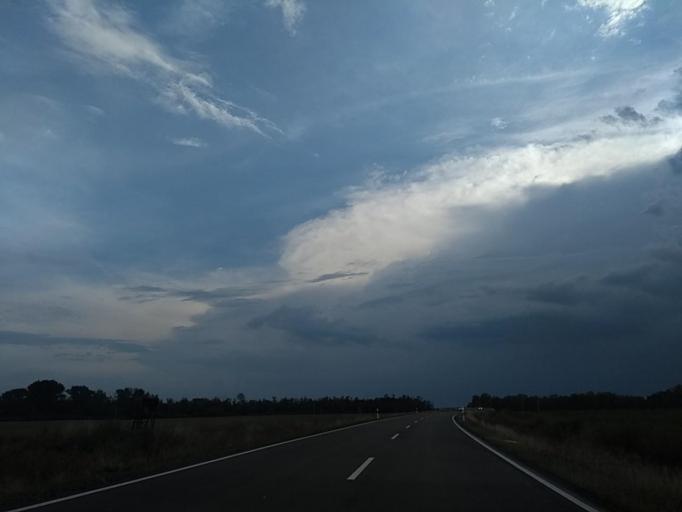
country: DE
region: Saxony-Anhalt
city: Hohenmolsen
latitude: 51.1687
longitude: 12.1194
